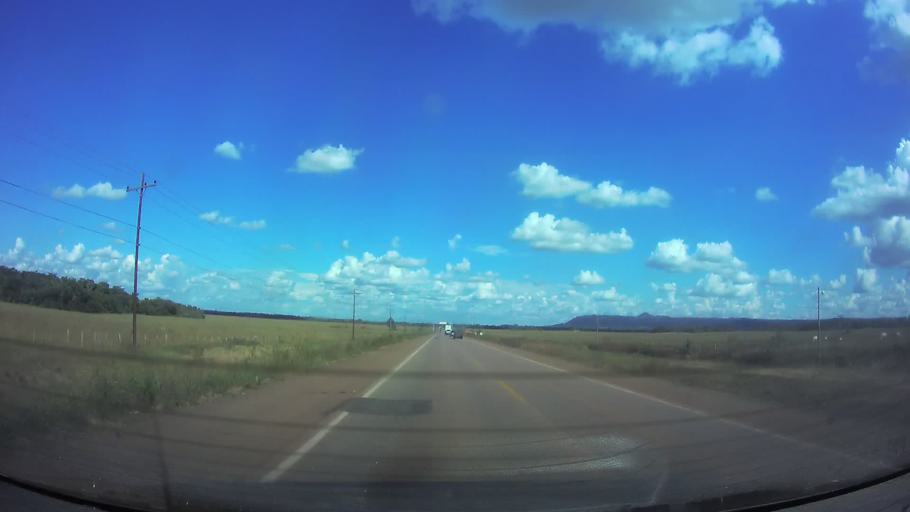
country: PY
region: Paraguari
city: Sapucai
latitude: -25.7012
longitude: -56.8506
